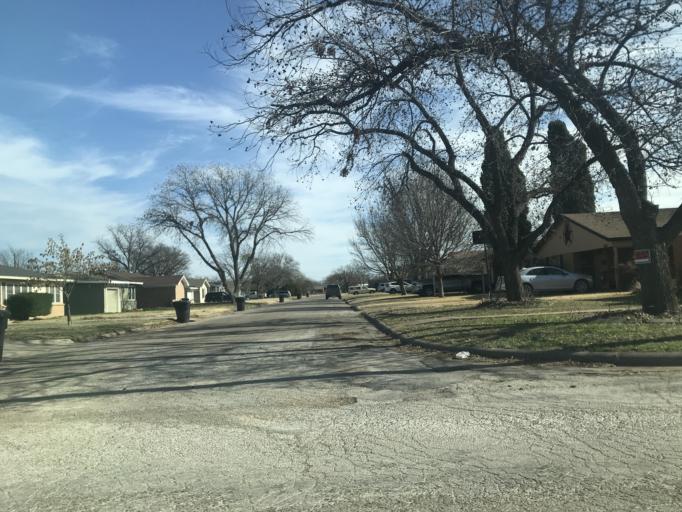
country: US
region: Texas
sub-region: Taylor County
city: Abilene
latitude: 32.4221
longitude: -99.7557
